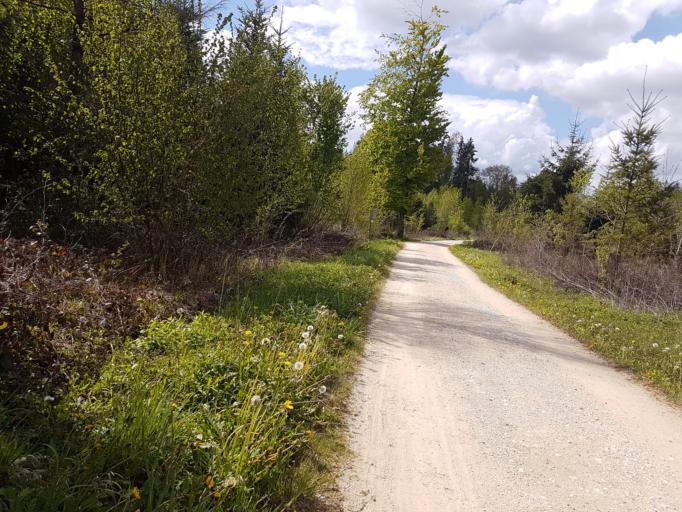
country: CH
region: Aargau
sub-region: Bezirk Zofingen
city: Fulenbach
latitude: 47.2946
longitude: 7.8488
